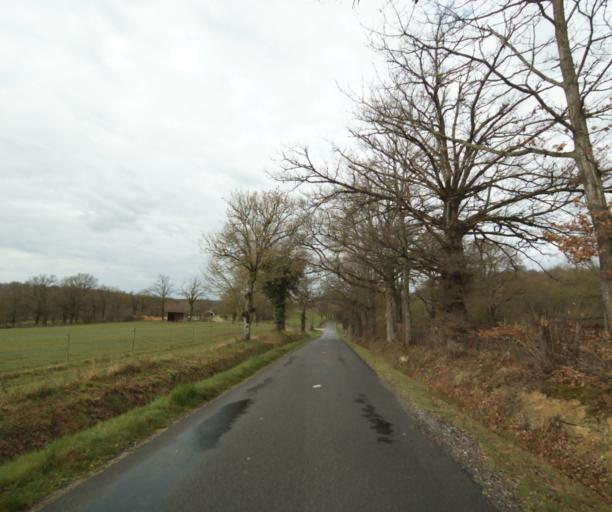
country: FR
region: Auvergne
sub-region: Departement de l'Allier
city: Toulon-sur-Allier
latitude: 46.5210
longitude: 3.3922
